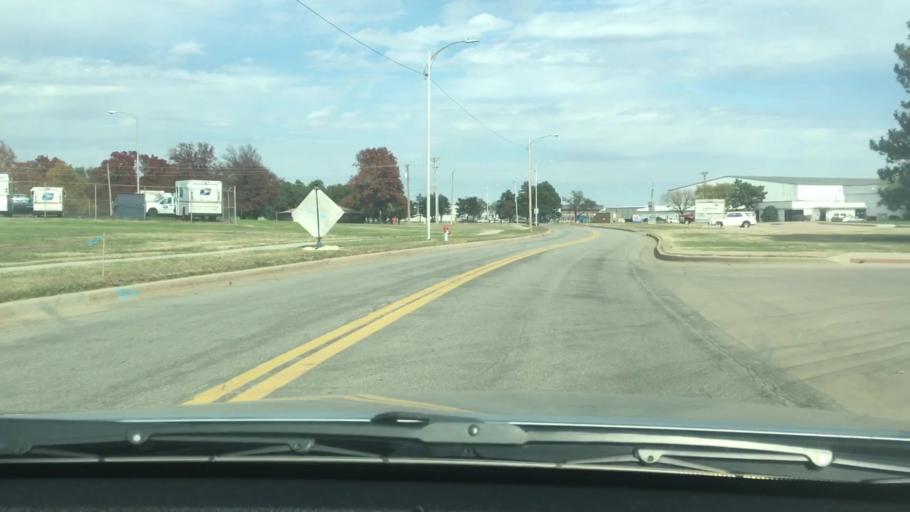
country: US
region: Kansas
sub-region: Sedgwick County
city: Wichita
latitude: 37.6639
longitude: -97.4225
